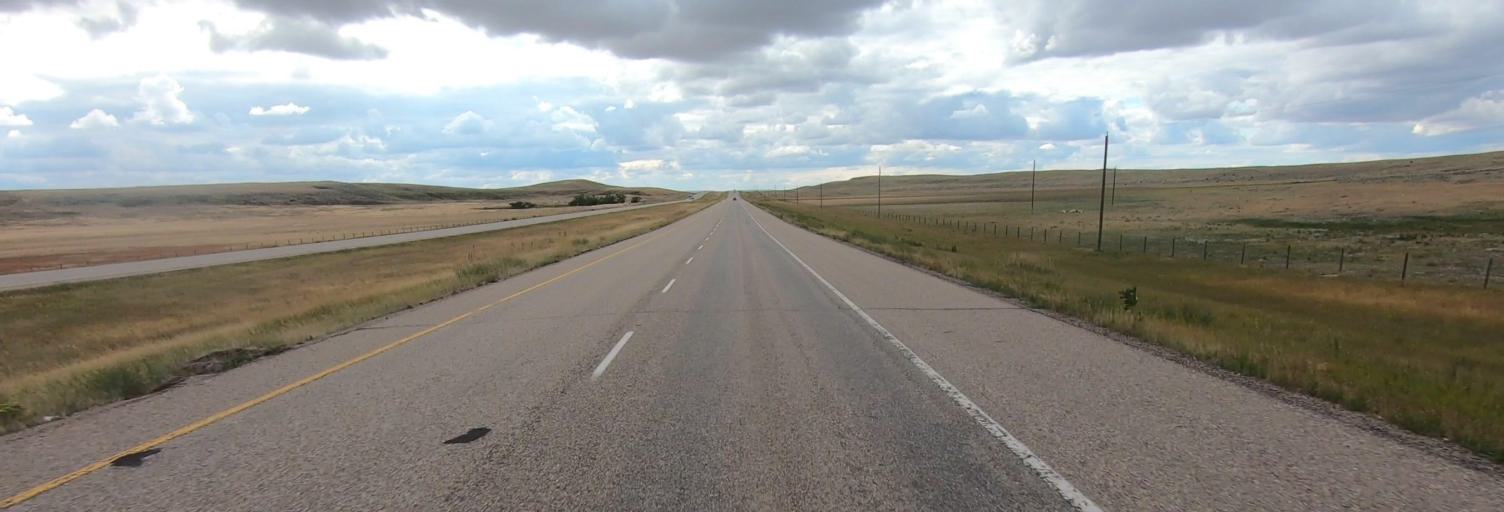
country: CA
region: Saskatchewan
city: Maple Creek
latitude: 49.9396
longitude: -110.0652
